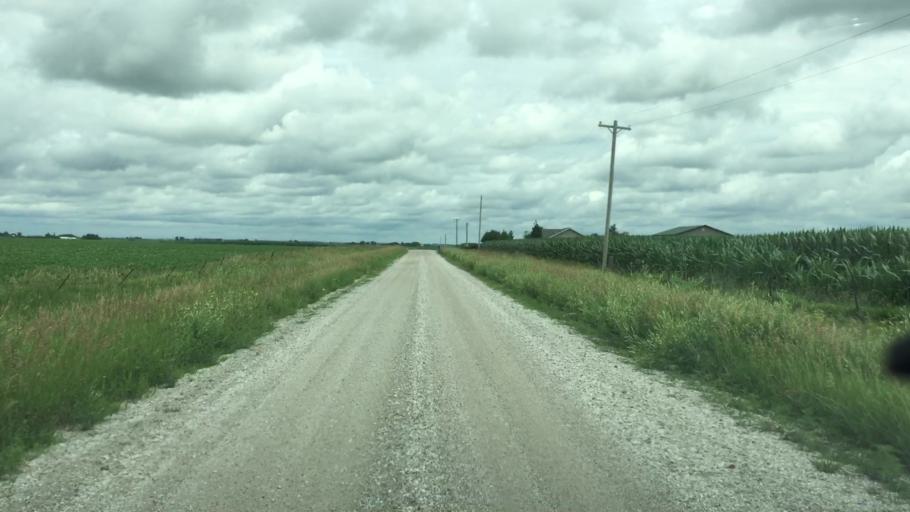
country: US
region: Iowa
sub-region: Jasper County
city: Monroe
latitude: 41.5738
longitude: -93.1208
